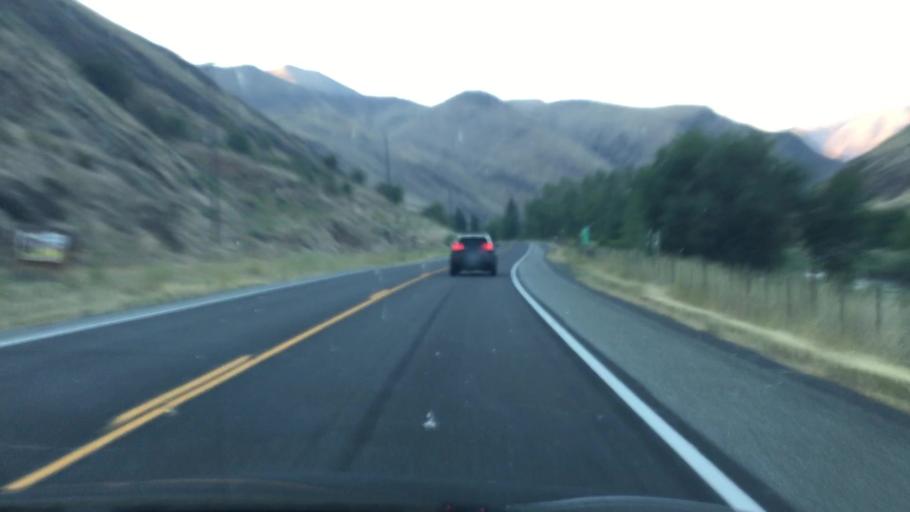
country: US
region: Idaho
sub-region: Valley County
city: McCall
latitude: 45.3844
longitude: -116.3506
